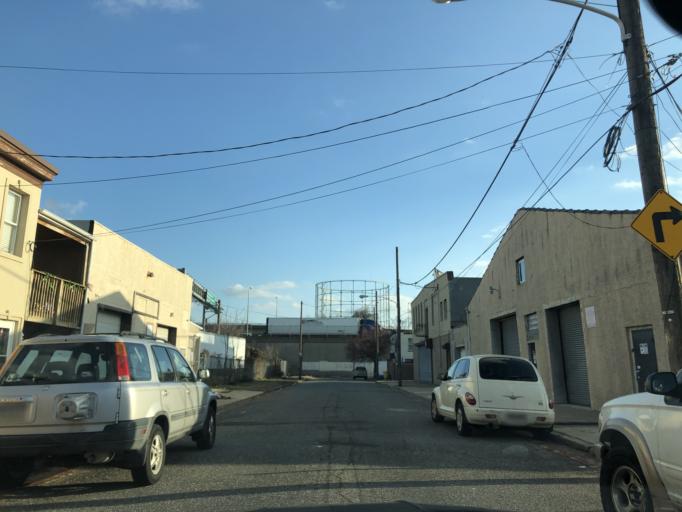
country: US
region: New Jersey
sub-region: Camden County
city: Pennsauken
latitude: 39.9883
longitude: -75.0908
